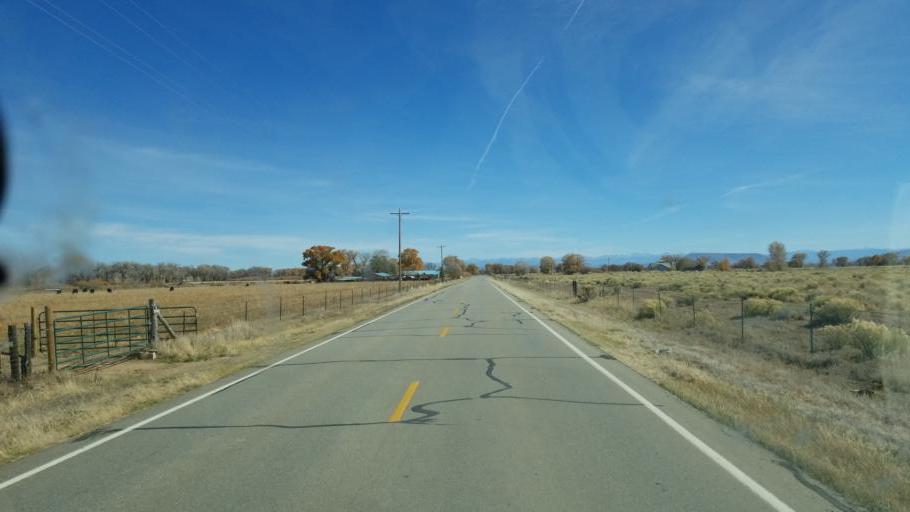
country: US
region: Colorado
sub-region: Conejos County
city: Conejos
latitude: 37.2836
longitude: -106.0977
